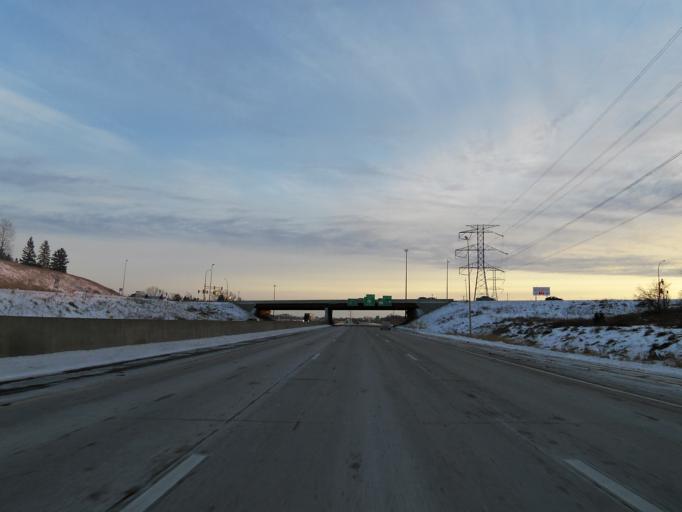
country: US
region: Minnesota
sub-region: Hennepin County
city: Eden Prairie
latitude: 44.8702
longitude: -93.4334
